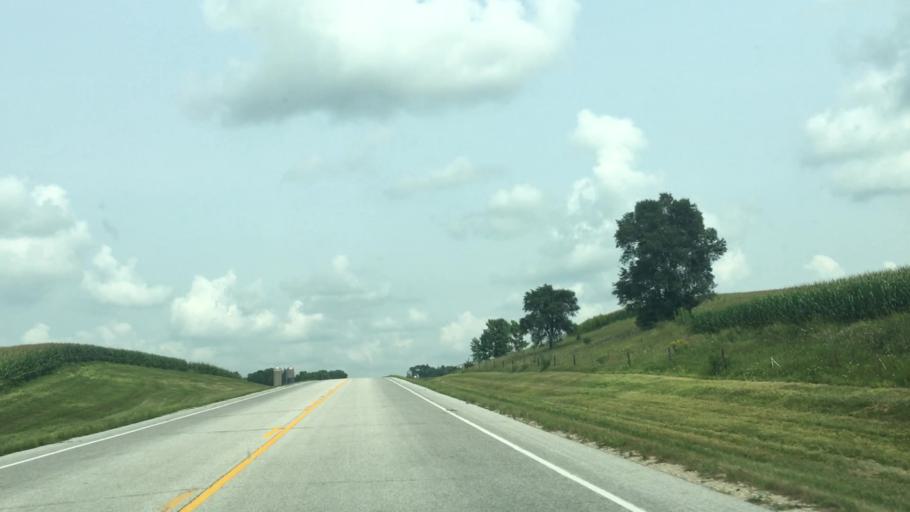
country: US
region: Minnesota
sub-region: Fillmore County
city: Harmony
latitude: 43.6076
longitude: -91.9297
